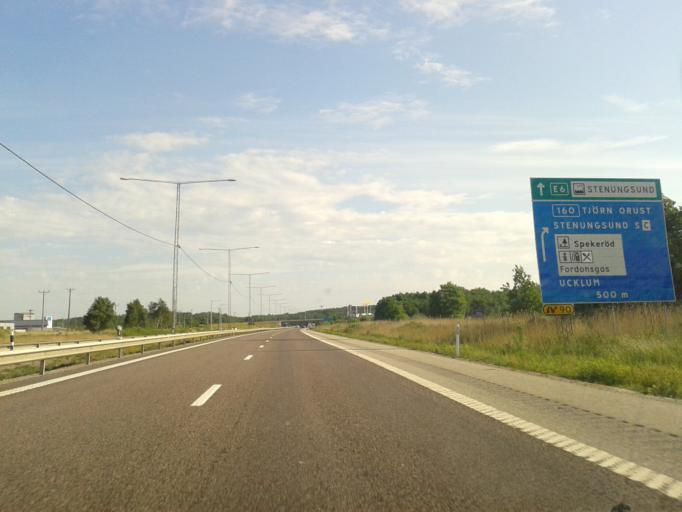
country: SE
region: Vaestra Goetaland
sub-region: Stenungsunds Kommun
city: Stora Hoga
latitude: 58.0192
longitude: 11.8441
